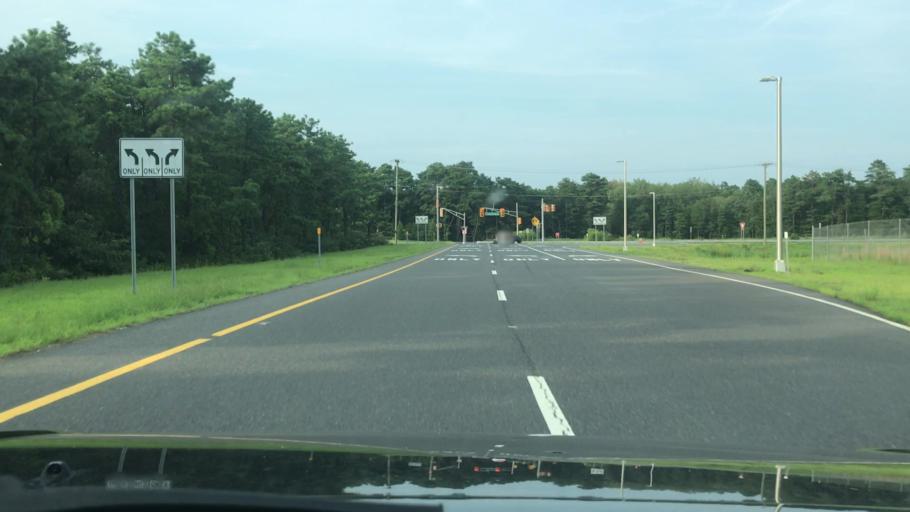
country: US
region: New Jersey
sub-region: Ocean County
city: Leisure Village
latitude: 40.0630
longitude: -74.1607
